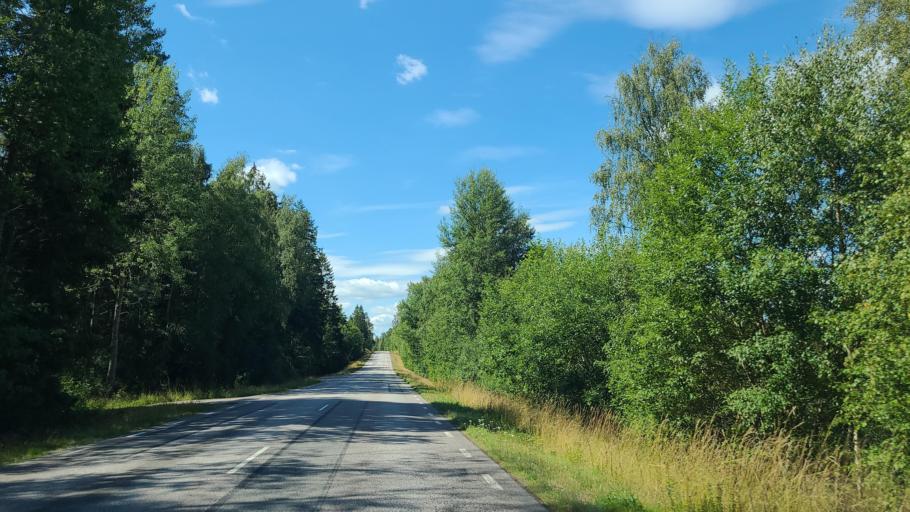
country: SE
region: Kalmar
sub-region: Emmaboda Kommun
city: Emmaboda
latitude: 56.5408
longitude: 15.6720
